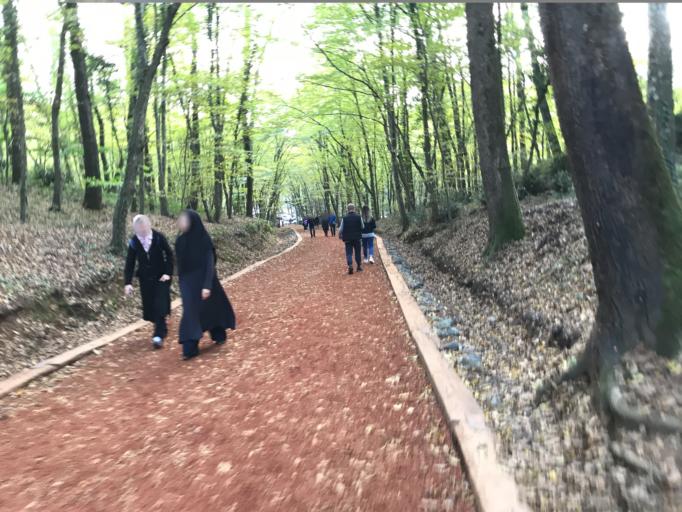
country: TR
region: Istanbul
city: Kemerburgaz
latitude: 41.1742
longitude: 28.9580
